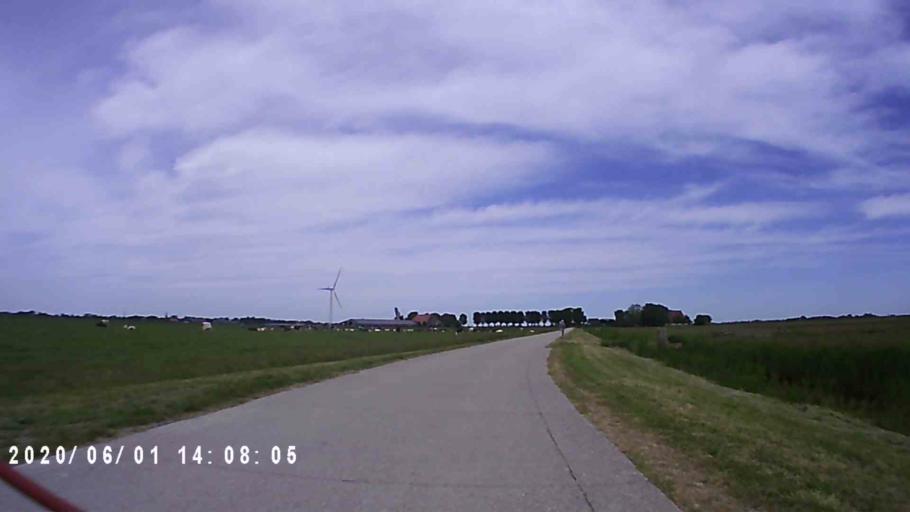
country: NL
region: Friesland
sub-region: Gemeente Littenseradiel
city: Winsum
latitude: 53.1195
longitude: 5.6413
